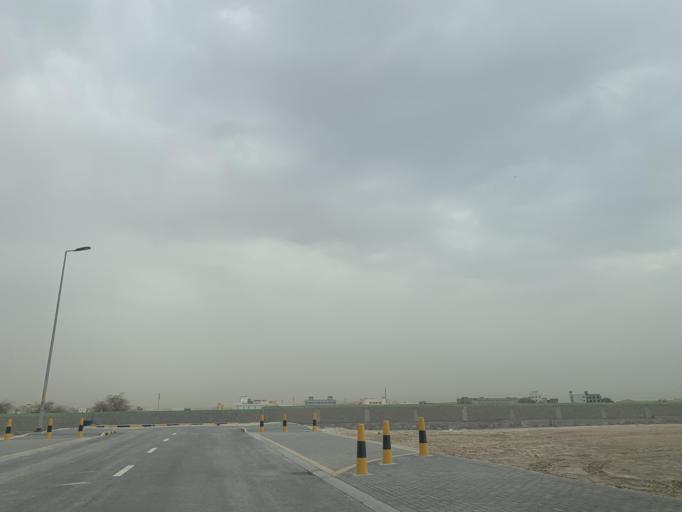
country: BH
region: Northern
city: Madinat `Isa
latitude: 26.1852
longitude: 50.5109
